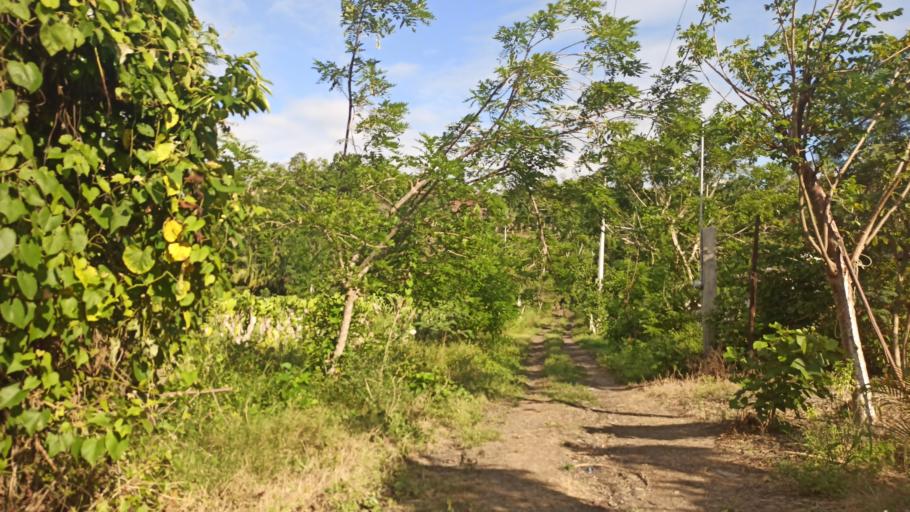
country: MX
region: Veracruz
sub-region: Papantla
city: Residencial Tajin
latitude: 20.6451
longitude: -97.3619
